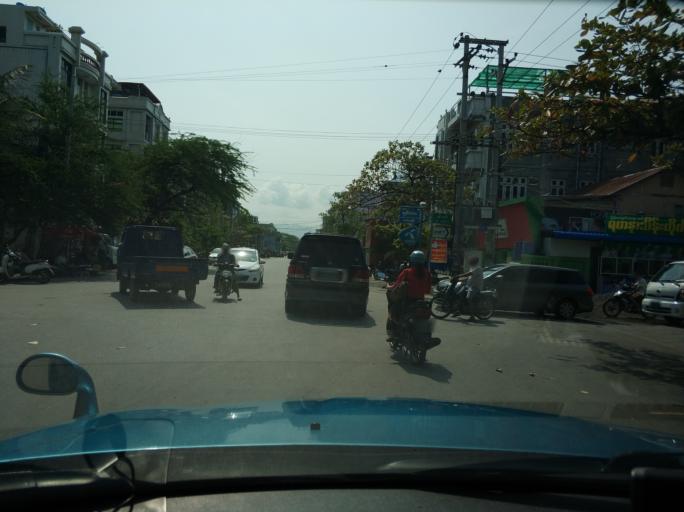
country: MM
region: Mandalay
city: Mandalay
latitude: 21.9736
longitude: 96.0902
